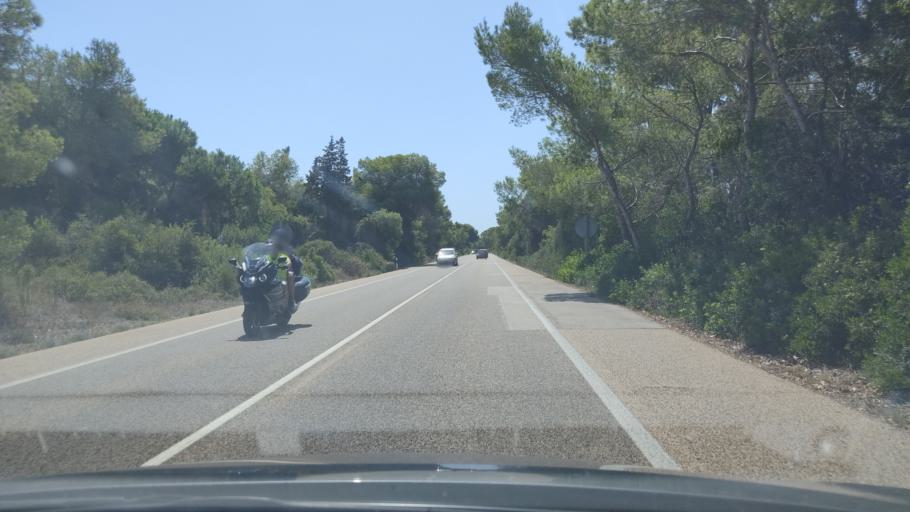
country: ES
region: Valencia
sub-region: Provincia de Valencia
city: Sollana
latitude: 39.3185
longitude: -0.3063
